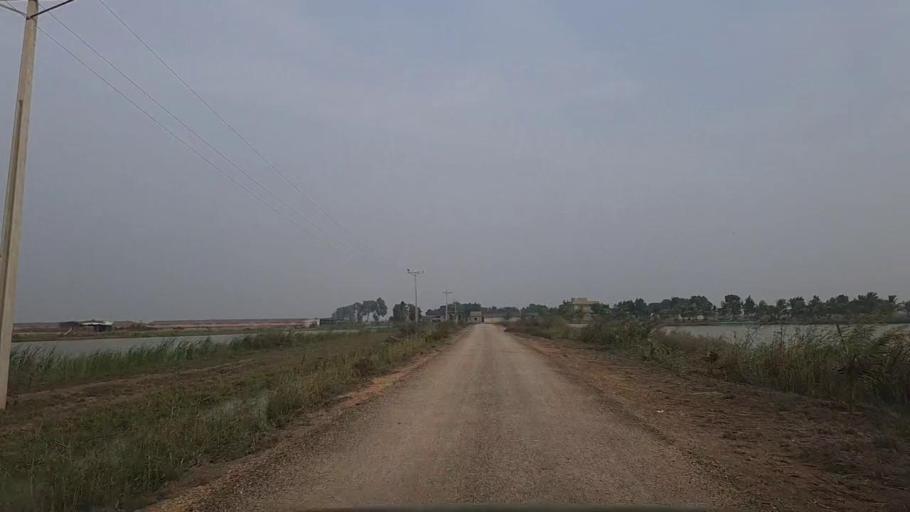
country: PK
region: Sindh
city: Chuhar Jamali
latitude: 24.5034
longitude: 67.8821
